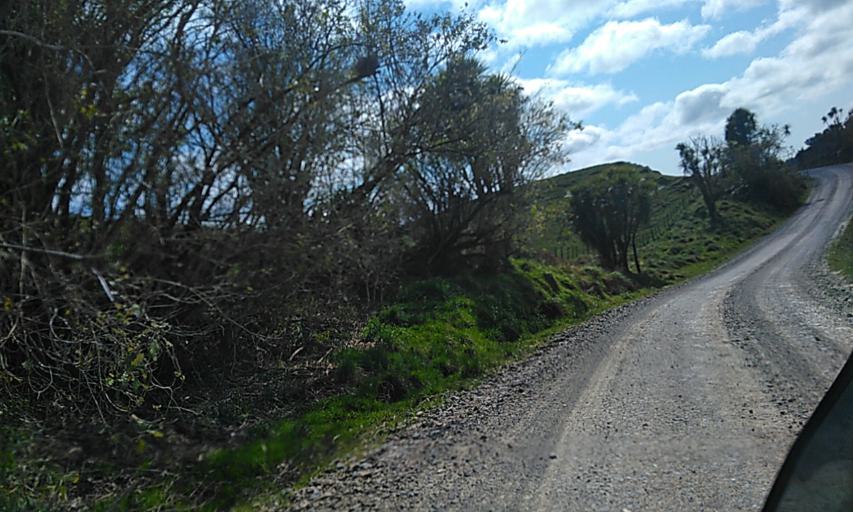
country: NZ
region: Gisborne
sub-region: Gisborne District
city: Gisborne
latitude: -38.2237
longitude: 178.0703
